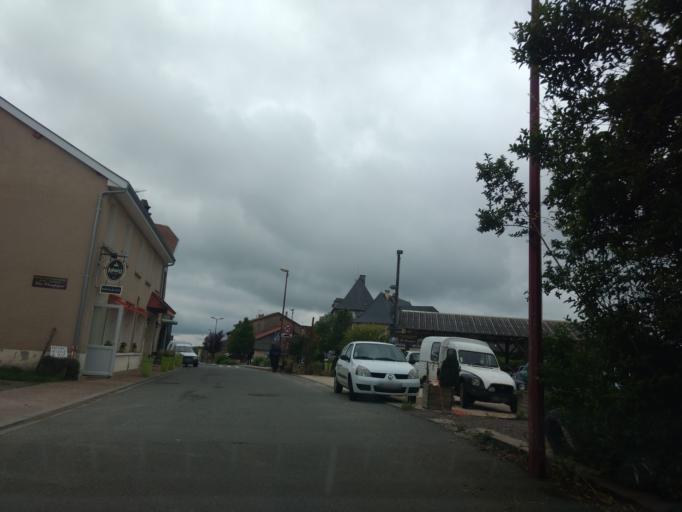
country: FR
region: Midi-Pyrenees
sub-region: Departement de l'Aveyron
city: Viviez
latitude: 44.5469
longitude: 2.1477
